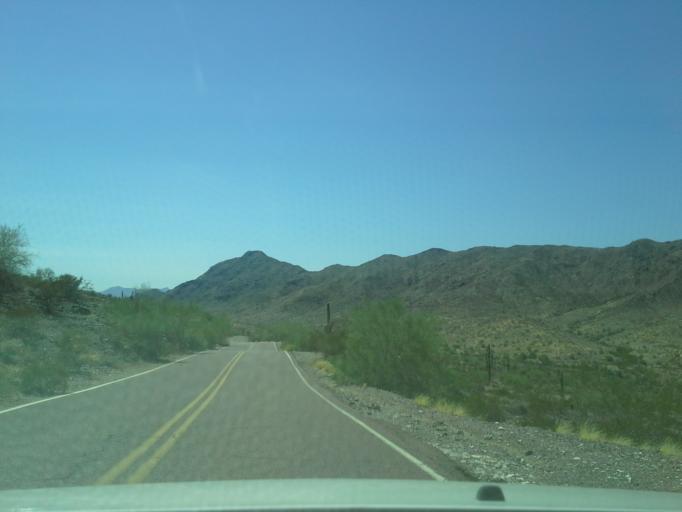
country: US
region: Arizona
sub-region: Maricopa County
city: Laveen
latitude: 33.3321
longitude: -112.0893
